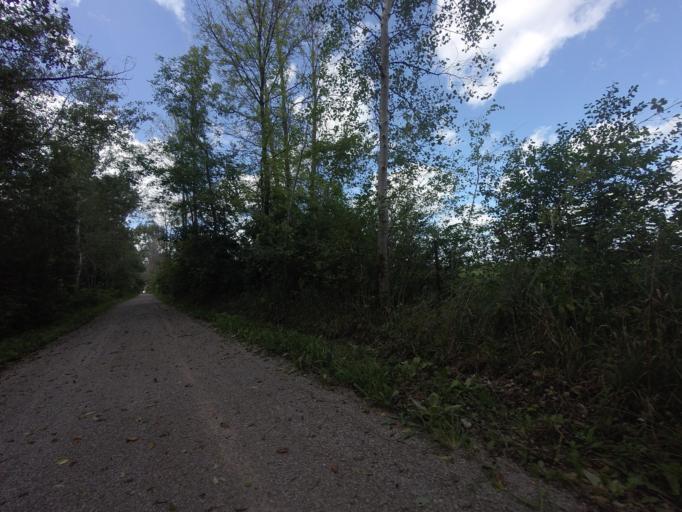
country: CA
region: Ontario
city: Huron East
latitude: 43.6381
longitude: -81.1972
